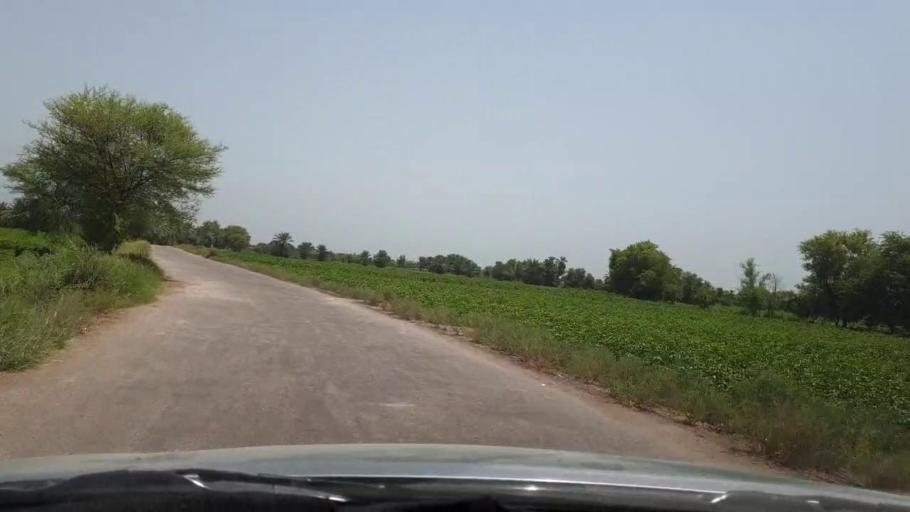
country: PK
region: Sindh
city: Pano Aqil
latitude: 27.8785
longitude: 69.1472
